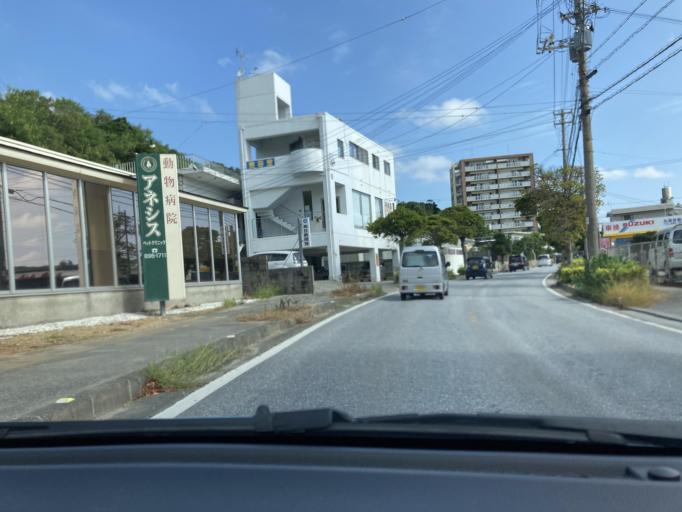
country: JP
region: Okinawa
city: Chatan
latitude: 26.2841
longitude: 127.7848
